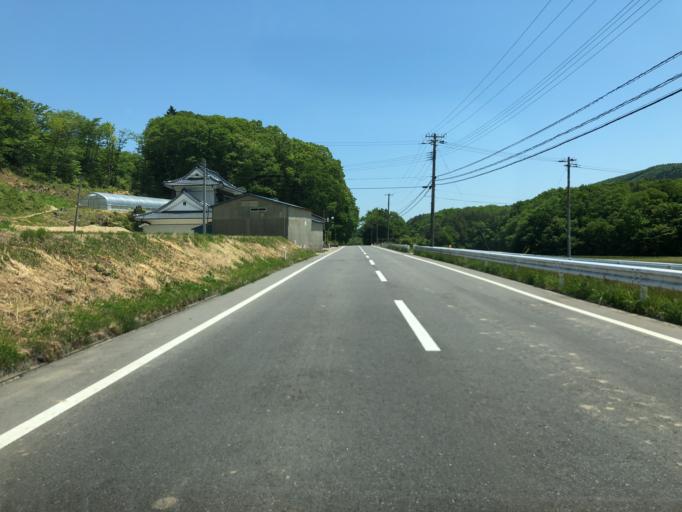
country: JP
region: Fukushima
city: Funehikimachi-funehiki
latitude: 37.5066
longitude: 140.7306
